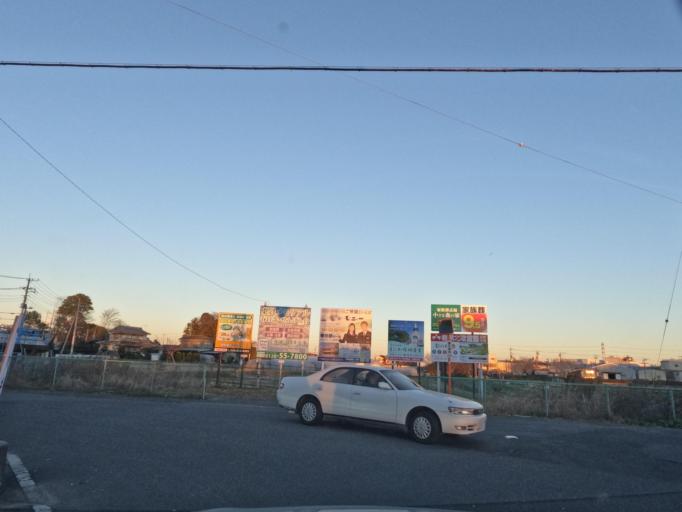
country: JP
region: Saitama
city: Kasukabe
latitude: 35.9823
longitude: 139.7269
